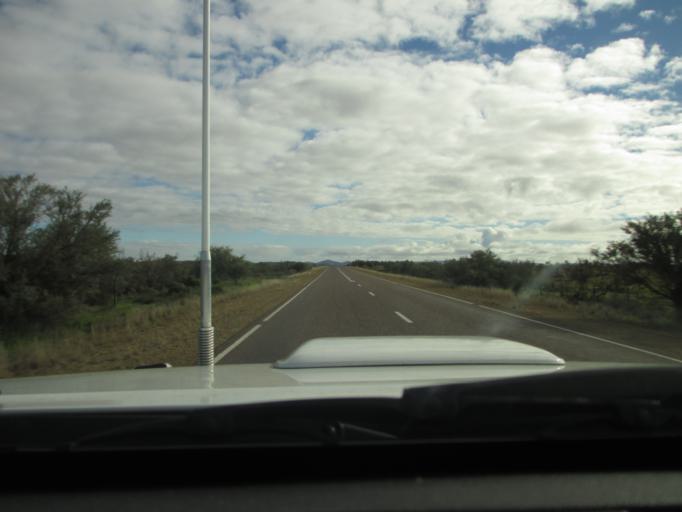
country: AU
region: South Australia
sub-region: Flinders Ranges
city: Quorn
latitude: -32.3505
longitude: 138.4884
